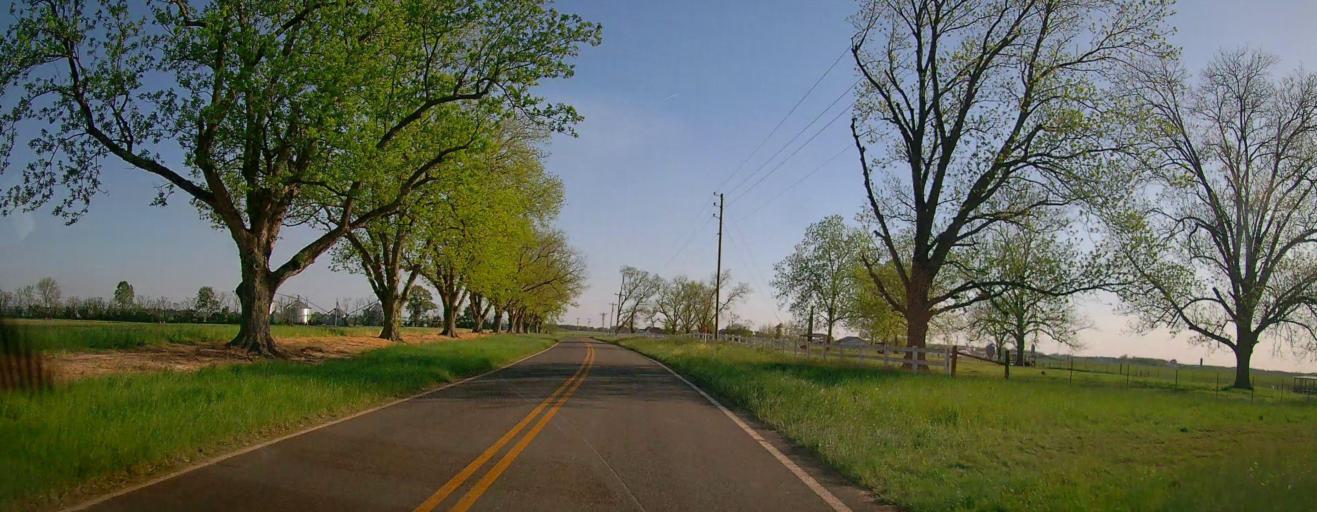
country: US
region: Georgia
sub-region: Macon County
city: Montezuma
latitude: 32.3284
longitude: -83.9624
